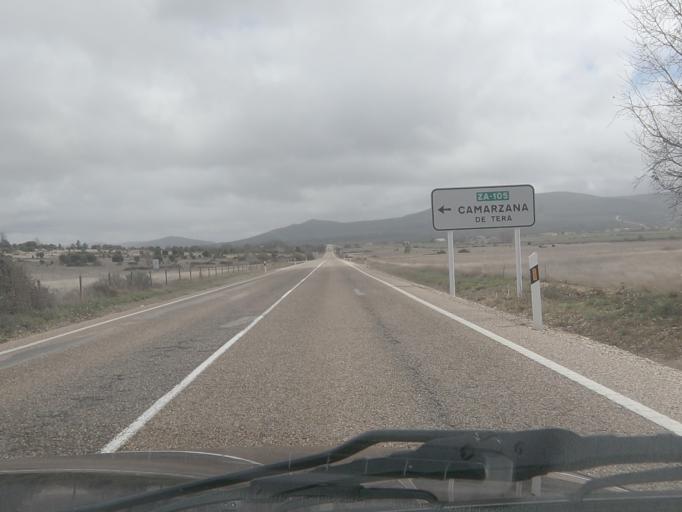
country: ES
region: Castille and Leon
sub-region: Provincia de Zamora
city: Ferreras de Abajo
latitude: 41.9130
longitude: -6.0823
